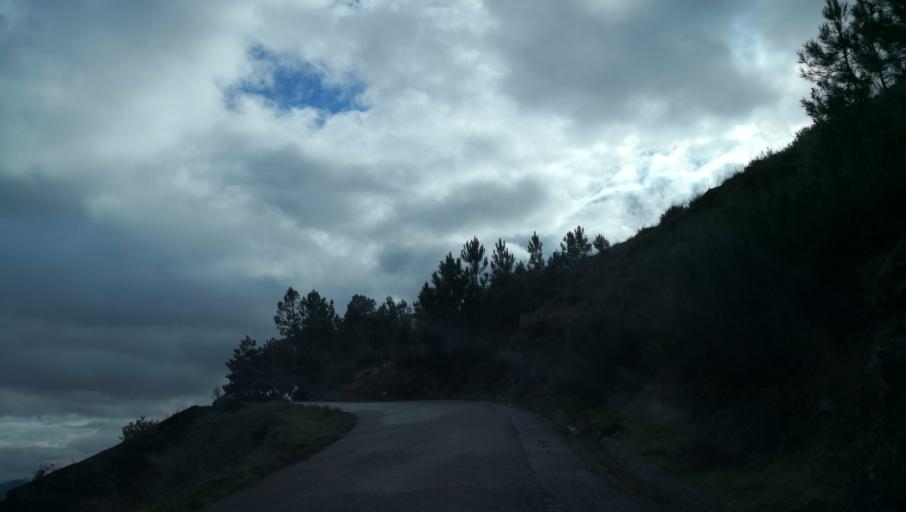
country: PT
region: Vila Real
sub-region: Sabrosa
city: Vilela
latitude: 41.1979
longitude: -7.5771
